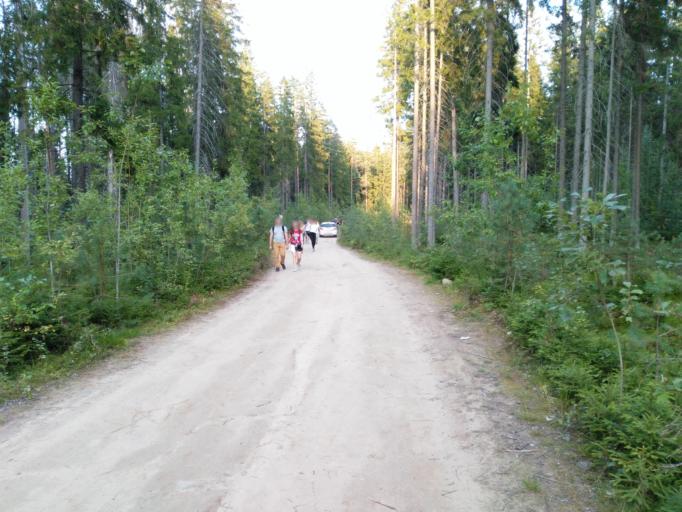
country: RU
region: Leningrad
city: Il'ichevo
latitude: 60.2789
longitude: 29.7504
